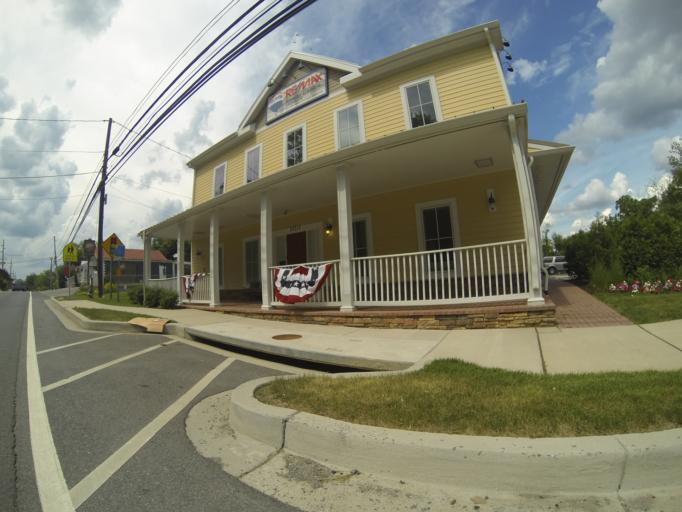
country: US
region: Maryland
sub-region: Montgomery County
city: Clarksburg
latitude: 39.2384
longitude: -77.2789
